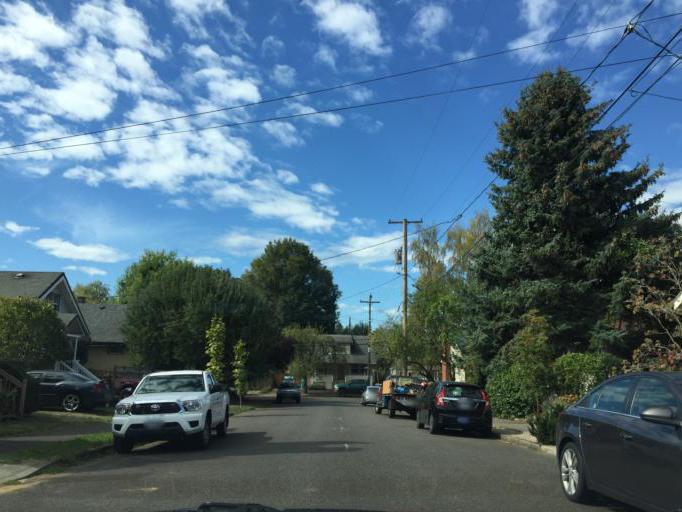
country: US
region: Oregon
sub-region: Clackamas County
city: Milwaukie
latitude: 45.4910
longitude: -122.6237
